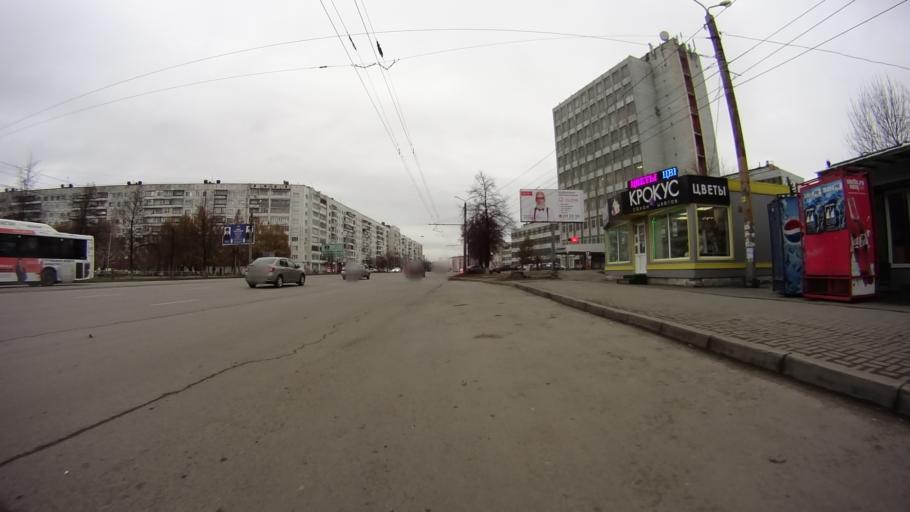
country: RU
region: Chelyabinsk
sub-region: Gorod Chelyabinsk
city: Chelyabinsk
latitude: 55.1940
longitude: 61.3549
